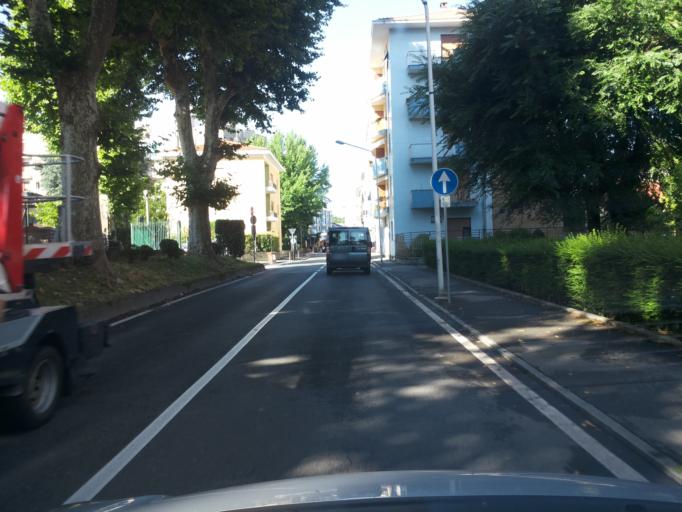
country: IT
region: Piedmont
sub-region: Provincia di Torino
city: Ivrea
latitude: 45.4700
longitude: 7.8875
